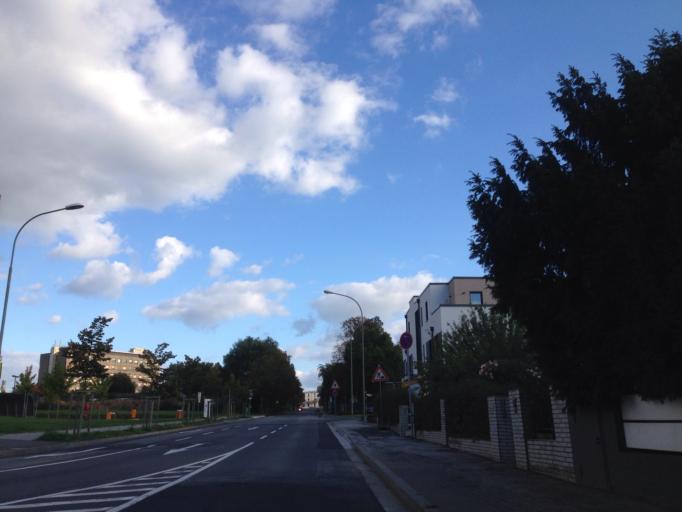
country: DE
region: Hesse
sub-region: Regierungsbezirk Giessen
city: Giessen
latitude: 50.5704
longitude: 8.6644
